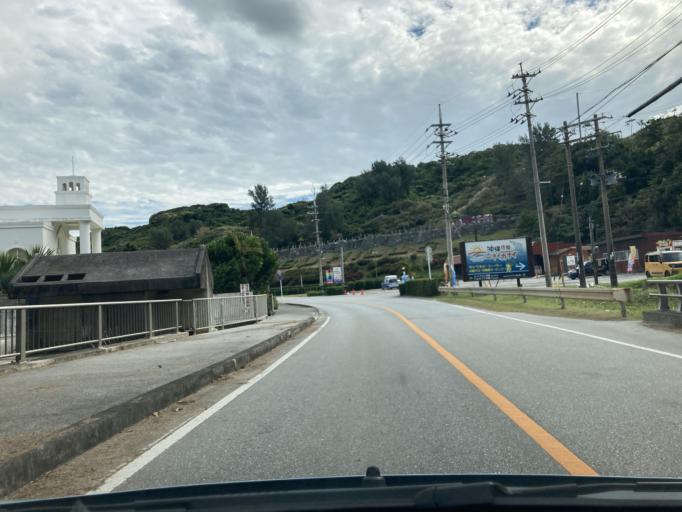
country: JP
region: Okinawa
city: Ishikawa
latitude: 26.4354
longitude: 127.7822
